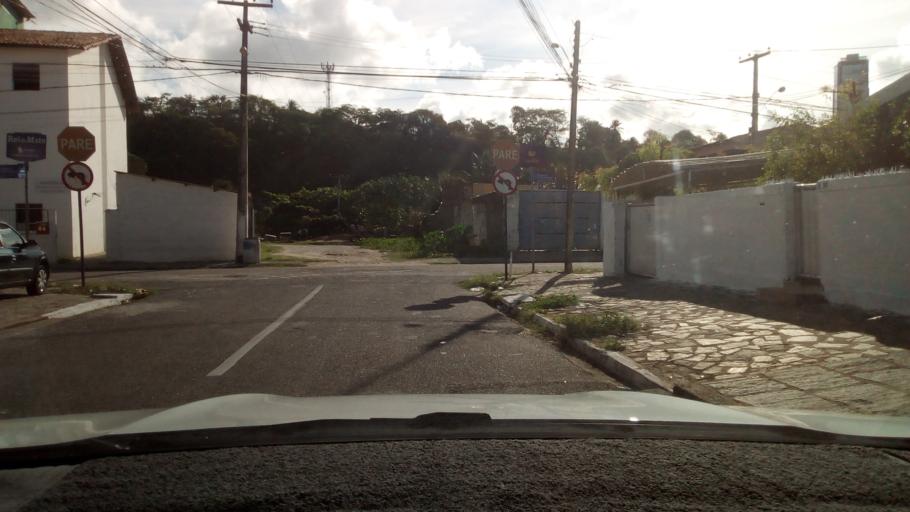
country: BR
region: Paraiba
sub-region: Joao Pessoa
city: Joao Pessoa
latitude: -7.1044
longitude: -34.8415
